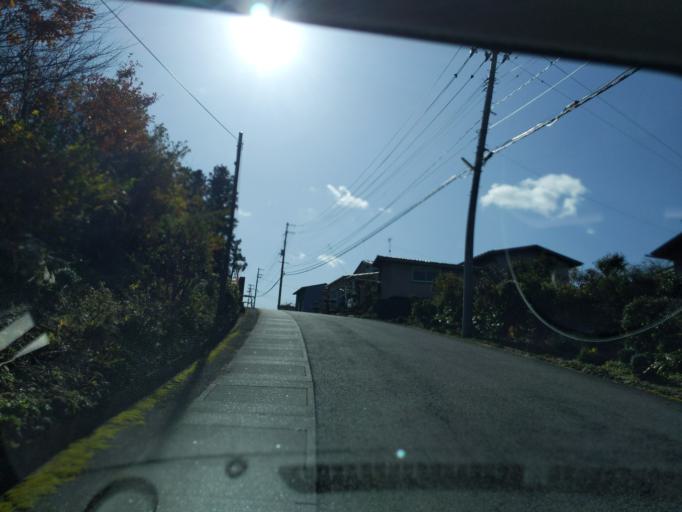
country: JP
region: Iwate
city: Mizusawa
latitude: 39.0345
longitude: 141.1137
